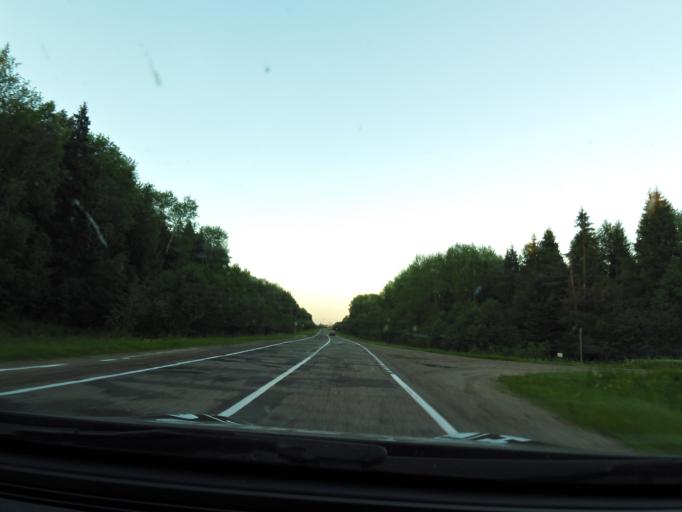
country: RU
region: Jaroslavl
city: Lyubim
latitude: 58.3557
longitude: 40.6334
